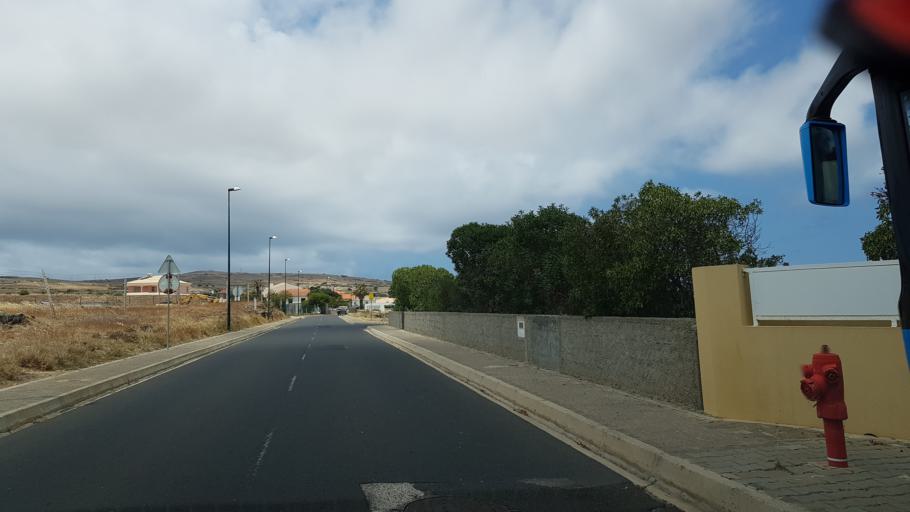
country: PT
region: Madeira
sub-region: Porto Santo
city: Vila de Porto Santo
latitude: 33.0623
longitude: -16.3367
